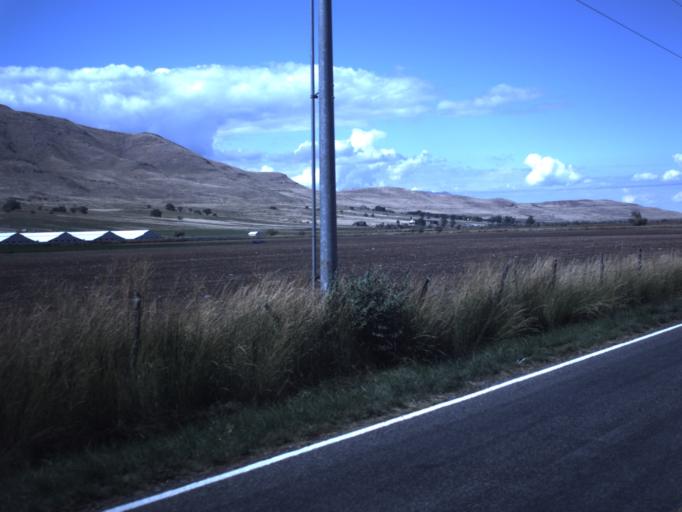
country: US
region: Utah
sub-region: Utah County
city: West Mountain
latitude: 40.0941
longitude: -111.7880
